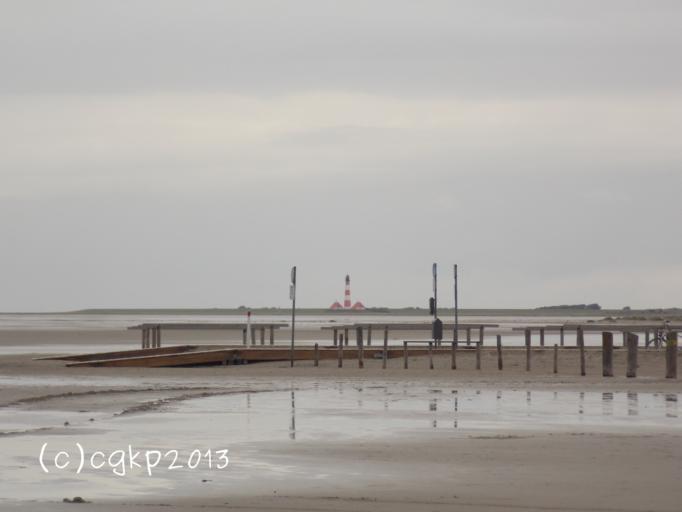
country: DE
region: Schleswig-Holstein
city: Sankt Peter-Ording
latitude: 54.3350
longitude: 8.5927
